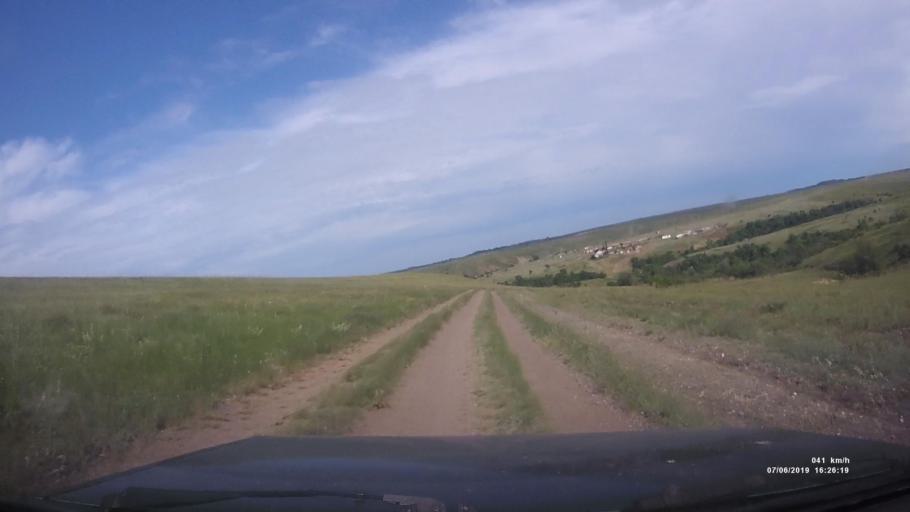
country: RU
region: Rostov
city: Kamensk-Shakhtinskiy
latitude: 48.2525
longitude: 40.3104
